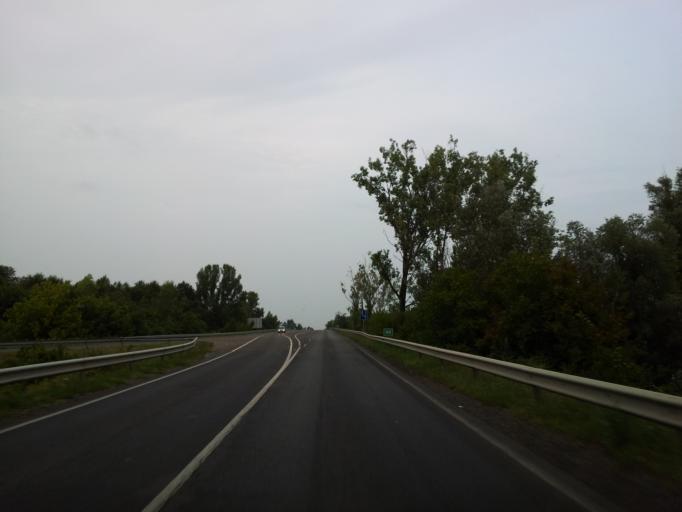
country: HU
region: Tolna
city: Szekszard
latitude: 46.3805
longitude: 18.7103
